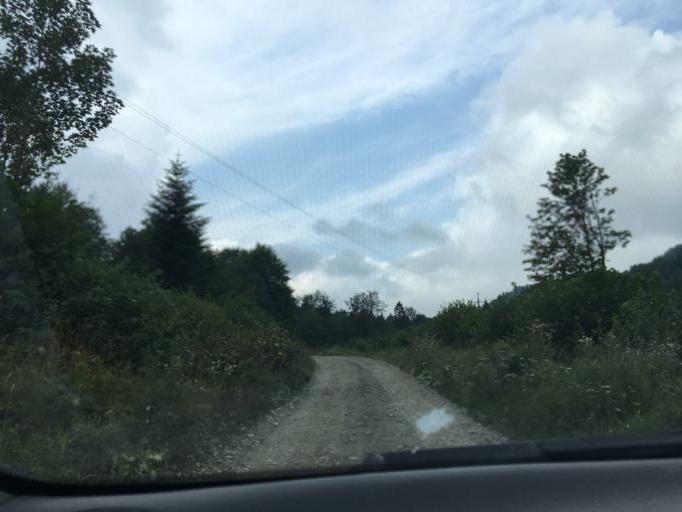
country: PL
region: Subcarpathian Voivodeship
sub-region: Powiat bieszczadzki
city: Lutowiska
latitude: 49.1920
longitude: 22.6147
